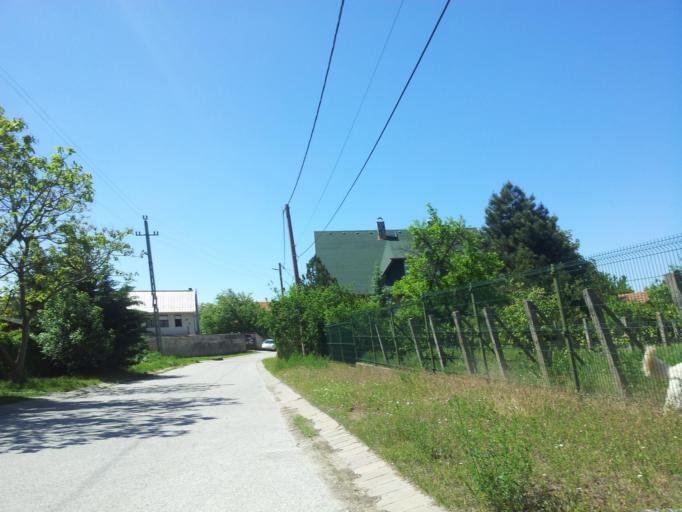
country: HU
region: Pest
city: Veresegyhaz
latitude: 47.6565
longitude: 19.2938
